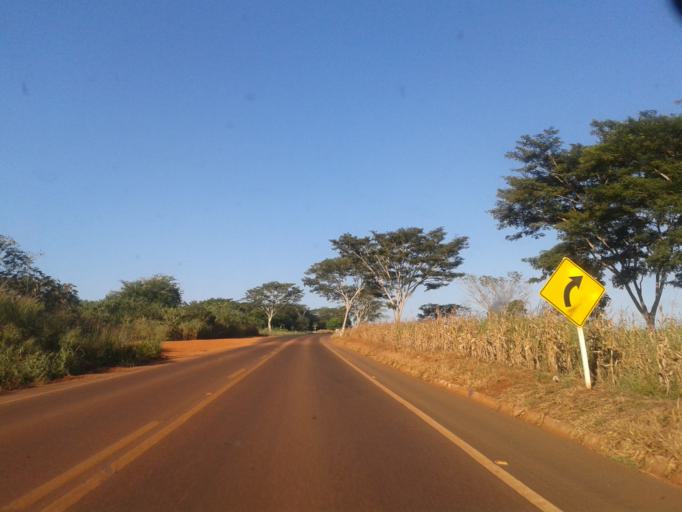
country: BR
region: Minas Gerais
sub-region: Santa Vitoria
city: Santa Vitoria
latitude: -18.6916
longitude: -49.9045
